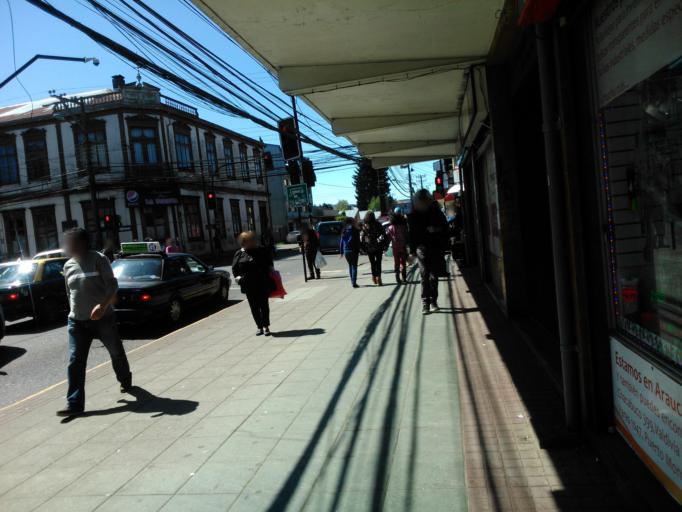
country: CL
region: Los Rios
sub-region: Provincia de Valdivia
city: Valdivia
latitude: -39.8154
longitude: -73.2446
